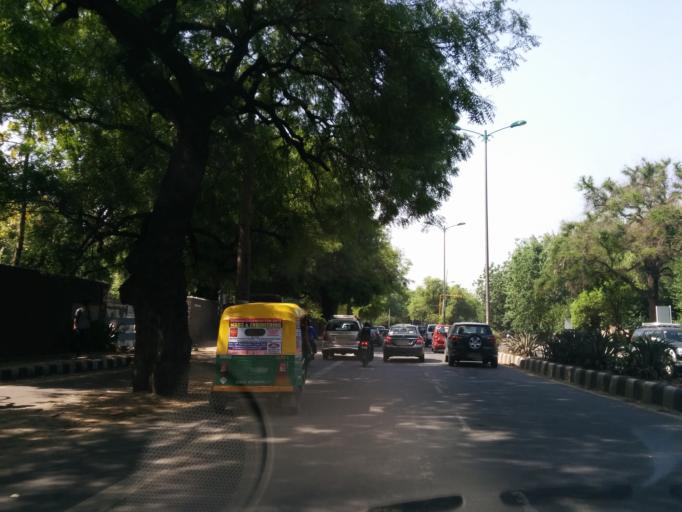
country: IN
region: NCT
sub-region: New Delhi
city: New Delhi
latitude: 28.5405
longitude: 77.1995
